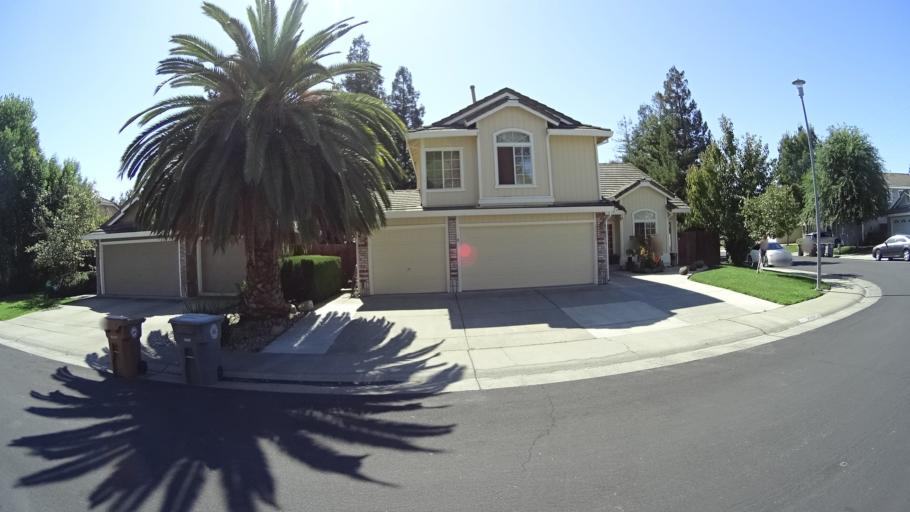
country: US
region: California
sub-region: Sacramento County
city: Laguna
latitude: 38.4353
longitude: -121.4348
